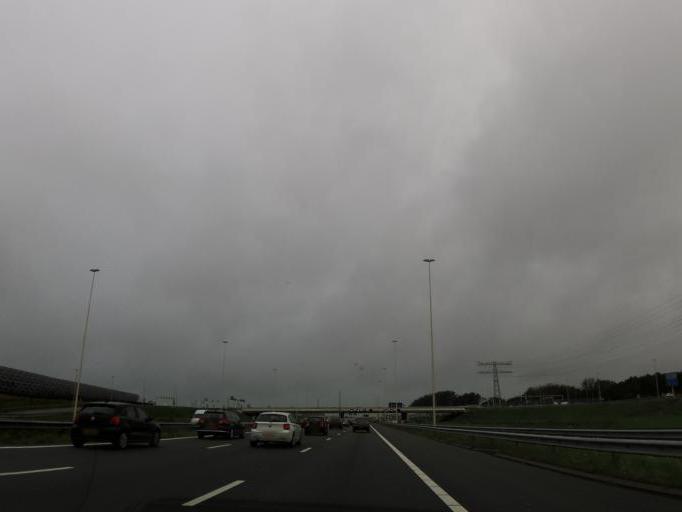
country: NL
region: Utrecht
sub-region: Stichtse Vecht
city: Maarssen
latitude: 52.1165
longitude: 5.0372
